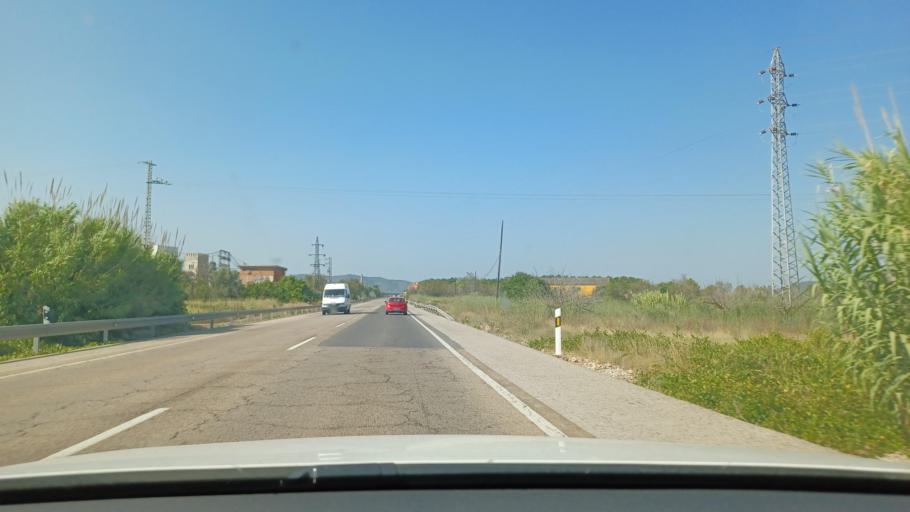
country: ES
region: Valencia
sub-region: Provincia de Castello
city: Alcala de Xivert
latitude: 40.3013
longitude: 0.2283
